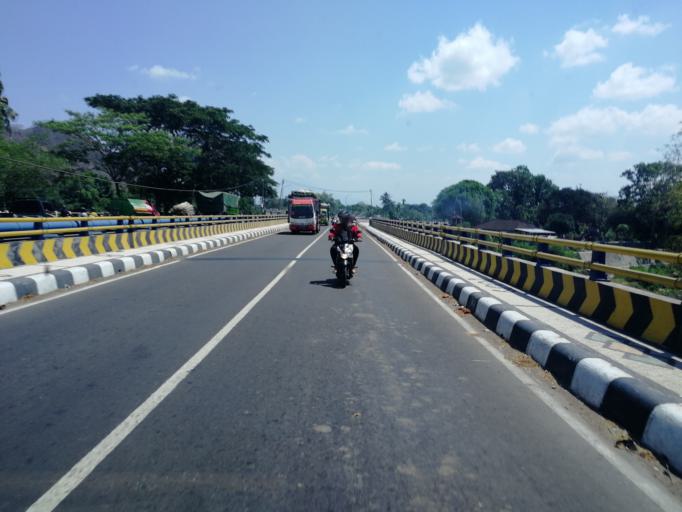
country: ID
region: West Nusa Tenggara
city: Karangkebon Timur
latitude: -8.6912
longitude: 116.1124
